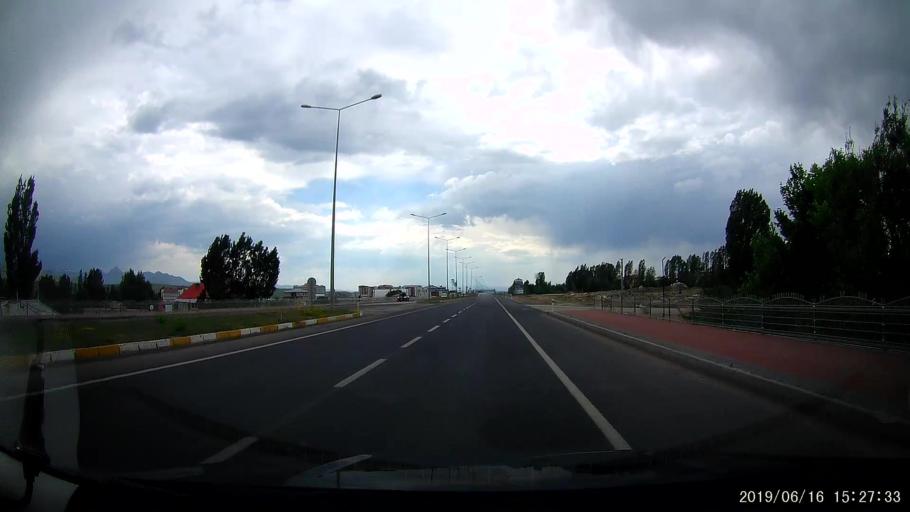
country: TR
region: Erzurum
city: Horasan
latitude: 40.0349
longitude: 42.1569
